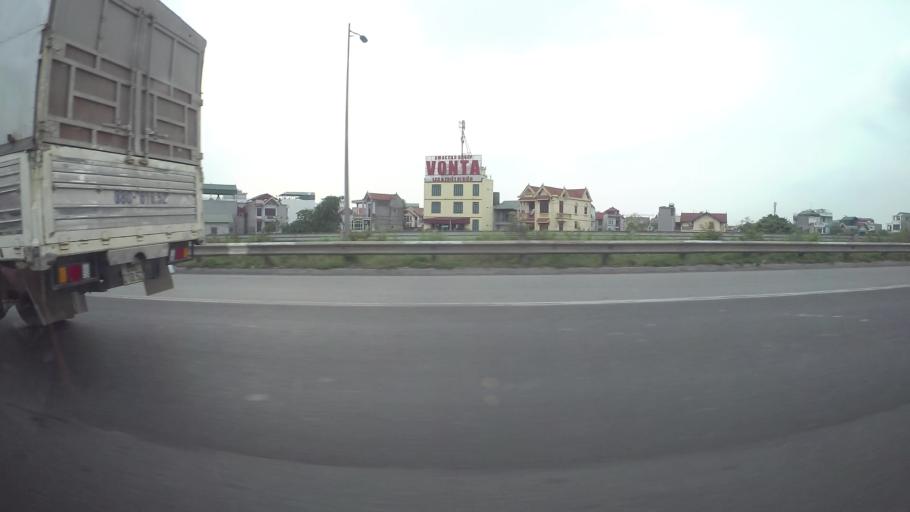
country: VN
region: Ha Noi
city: Trau Quy
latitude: 21.0150
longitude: 105.9198
